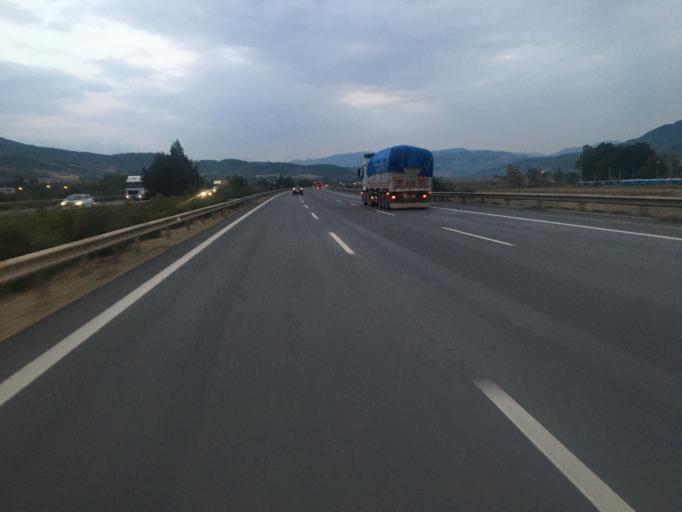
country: TR
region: Osmaniye
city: Osmaniye
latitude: 37.1367
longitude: 36.3140
